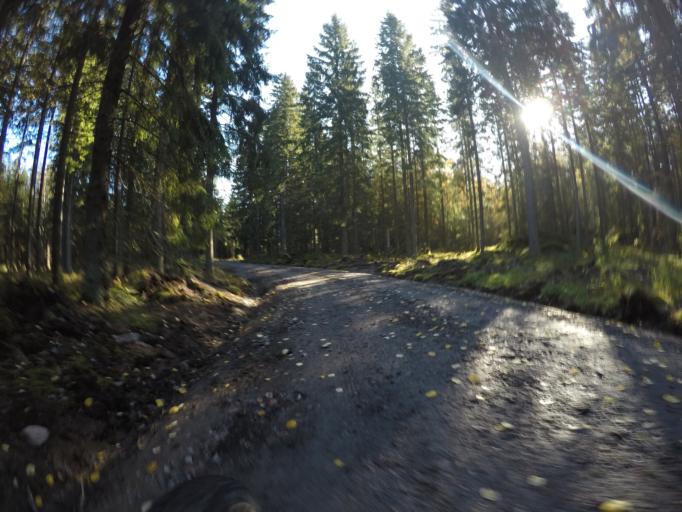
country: SE
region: Vaestmanland
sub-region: Kungsors Kommun
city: Kungsoer
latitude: 59.3098
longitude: 16.1001
